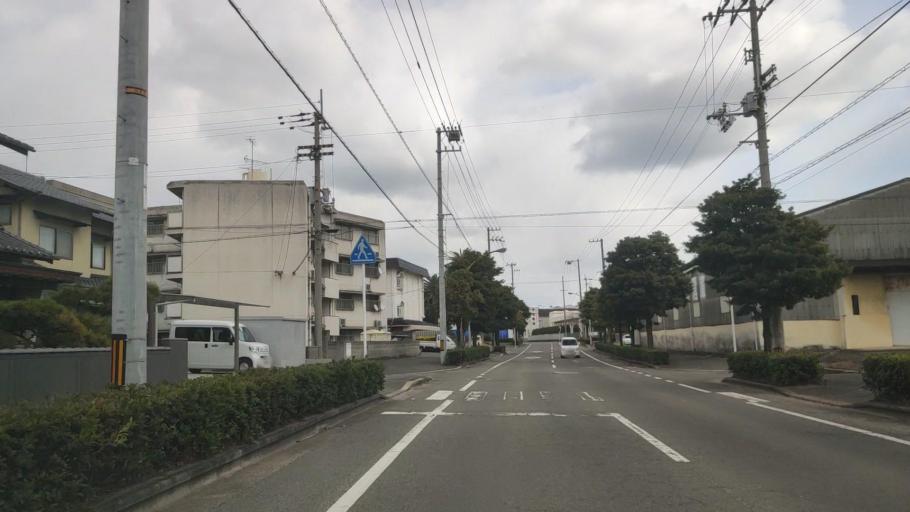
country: JP
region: Ehime
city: Saijo
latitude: 34.0564
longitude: 133.0195
